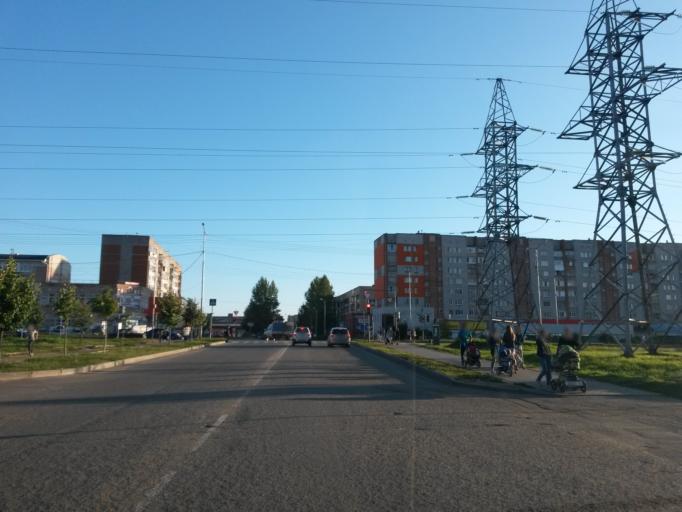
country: RU
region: Jaroslavl
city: Tutayev
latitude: 57.8647
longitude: 39.5131
